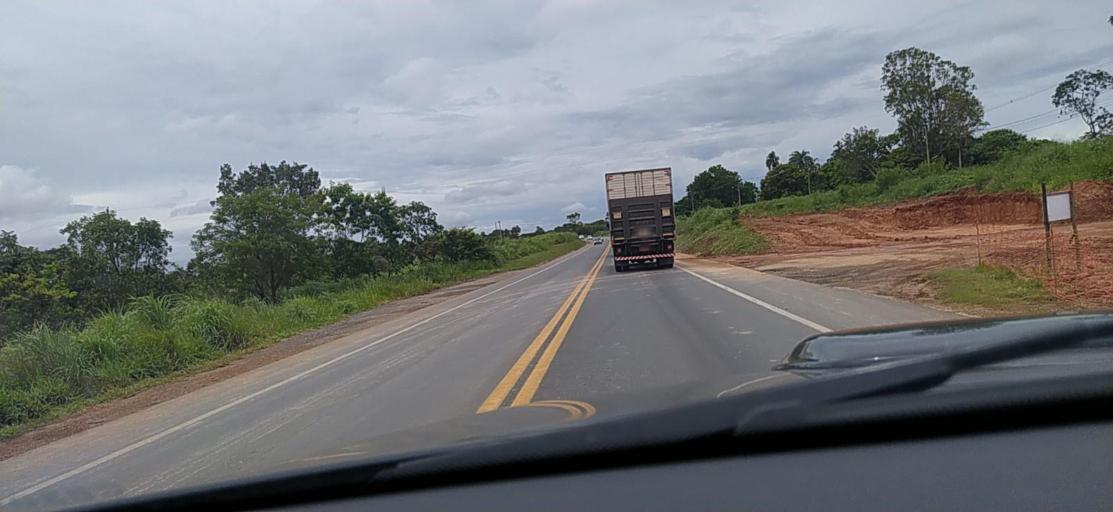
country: BR
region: Minas Gerais
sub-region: Curvelo
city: Curvelo
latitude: -18.7262
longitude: -44.4421
